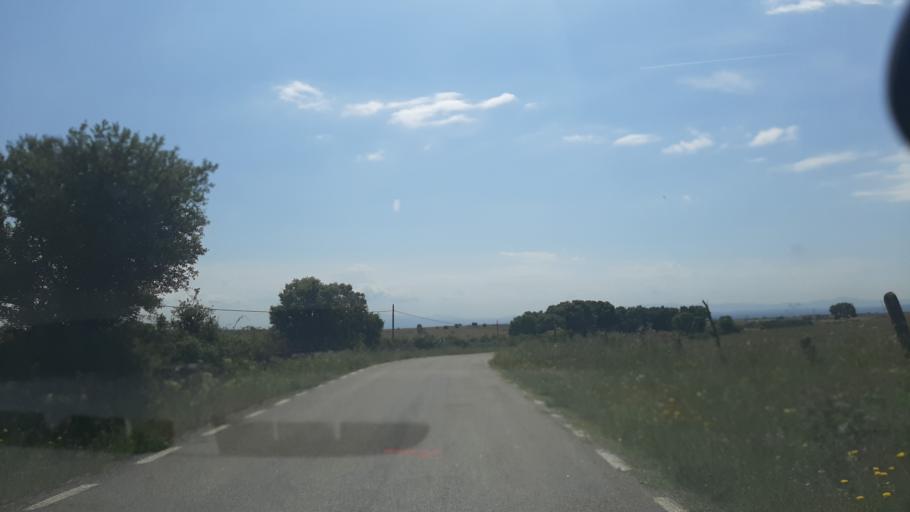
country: ES
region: Castille and Leon
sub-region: Provincia de Salamanca
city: Gallegos de Arganan
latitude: 40.6413
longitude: -6.7321
